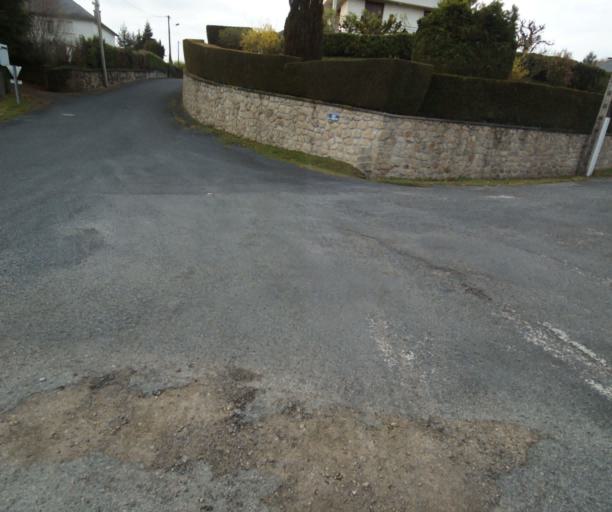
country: FR
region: Limousin
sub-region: Departement de la Correze
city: Correze
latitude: 45.3762
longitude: 1.8701
